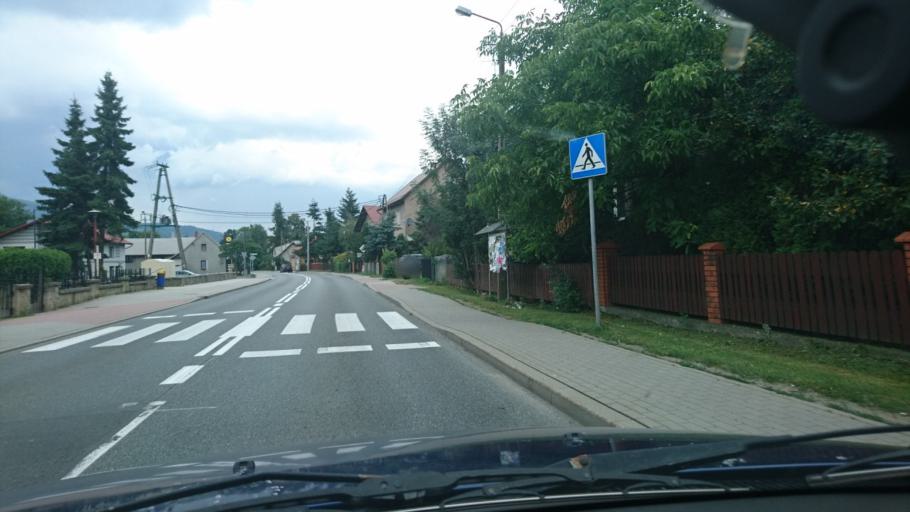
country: PL
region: Silesian Voivodeship
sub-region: Powiat zywiecki
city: Cisiec
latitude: 49.5849
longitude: 19.1028
